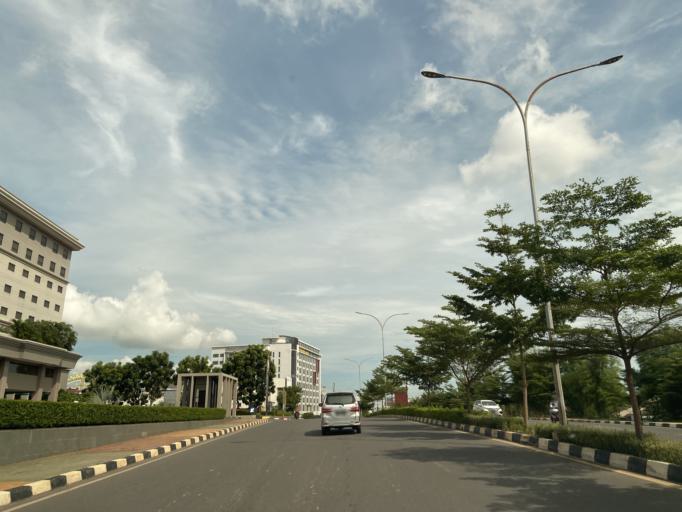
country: SG
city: Singapore
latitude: 1.1474
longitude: 104.0154
